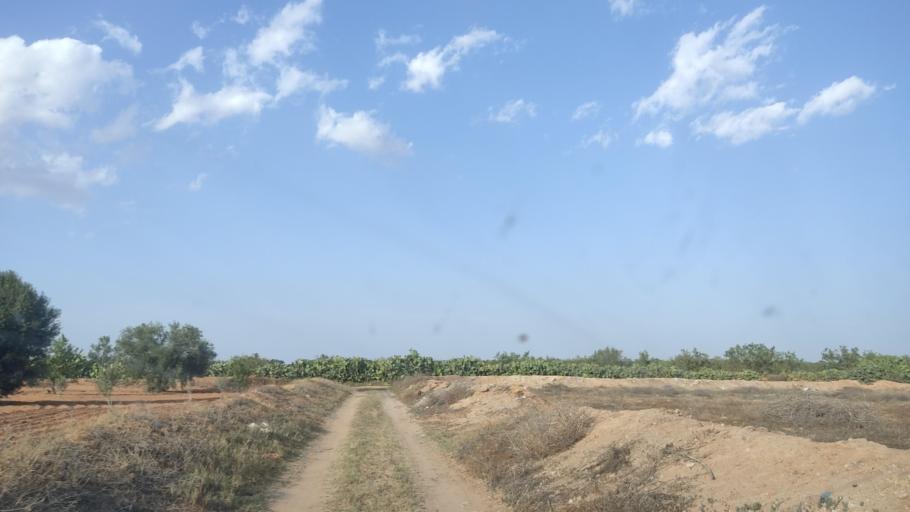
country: TN
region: Safaqis
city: Sfax
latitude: 34.8489
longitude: 10.5935
